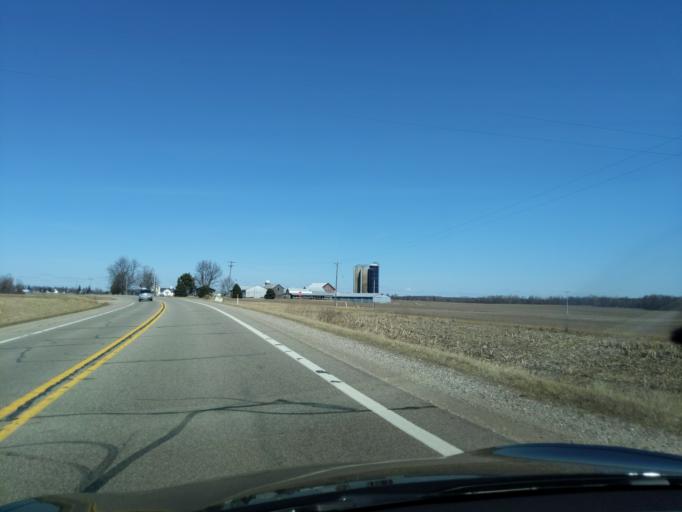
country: US
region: Michigan
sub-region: Ionia County
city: Lake Odessa
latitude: 42.7405
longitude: -85.0752
